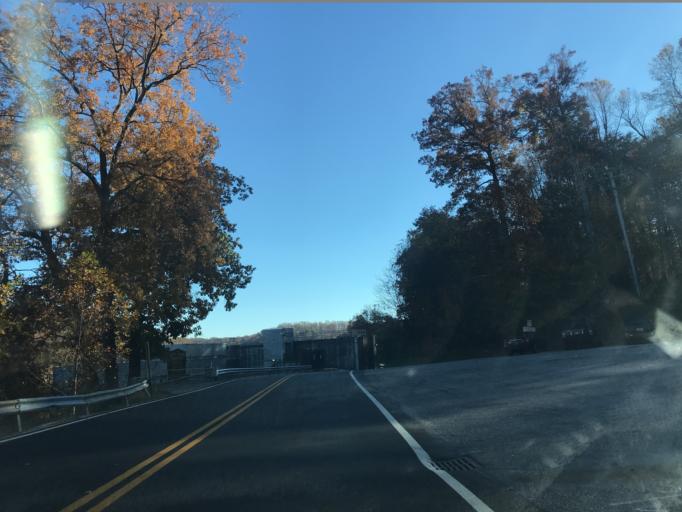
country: US
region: Maryland
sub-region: Baltimore County
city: Hampton
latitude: 39.4315
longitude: -76.5450
